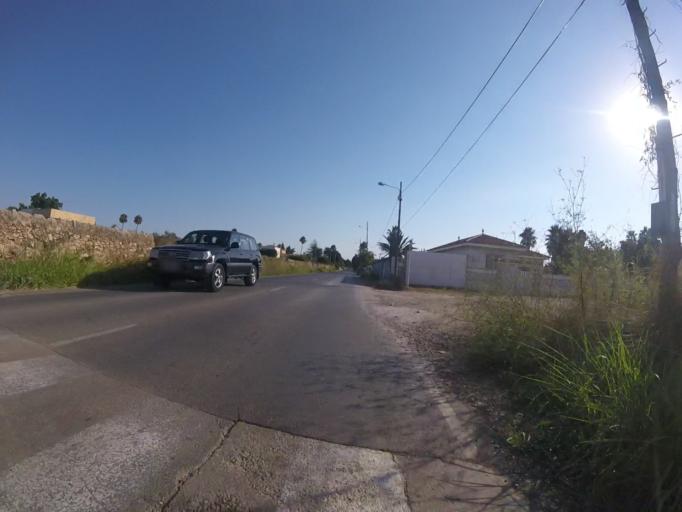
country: ES
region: Valencia
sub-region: Provincia de Castello
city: Benicarlo
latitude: 40.4076
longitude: 0.4179
